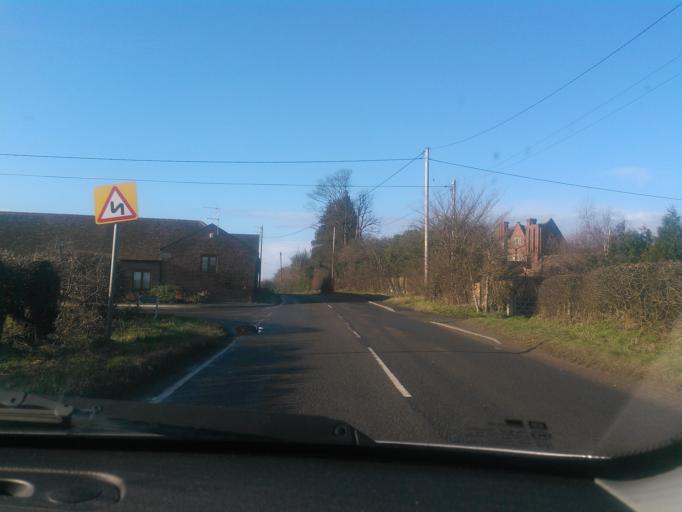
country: GB
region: England
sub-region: Telford and Wrekin
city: Eyton upon the Weald Moors
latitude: 52.7343
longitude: -2.5592
